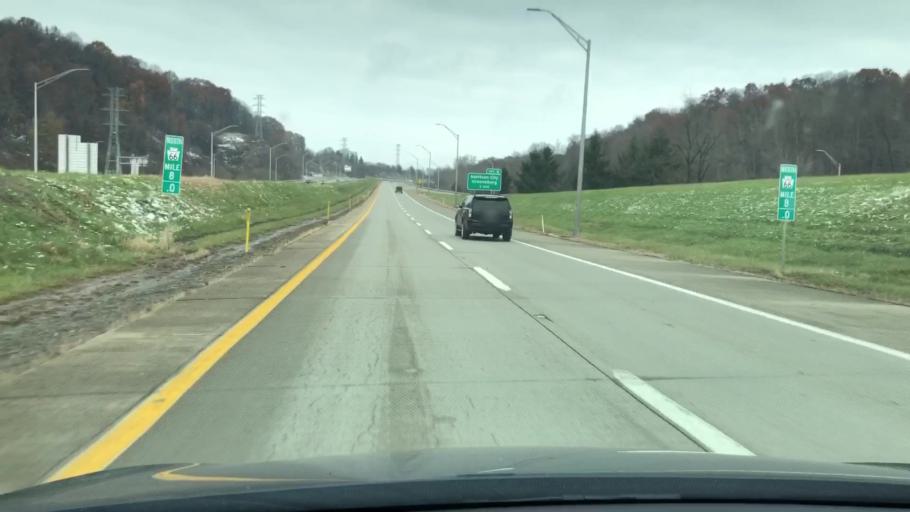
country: US
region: Pennsylvania
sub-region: Westmoreland County
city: Jeannette
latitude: 40.3283
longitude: -79.5797
